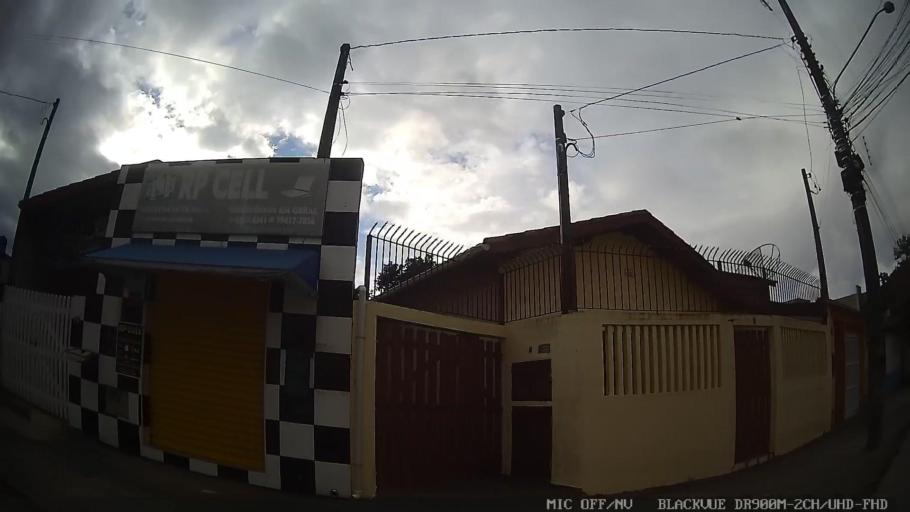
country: BR
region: Sao Paulo
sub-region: Itanhaem
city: Itanhaem
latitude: -24.1790
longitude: -46.7862
